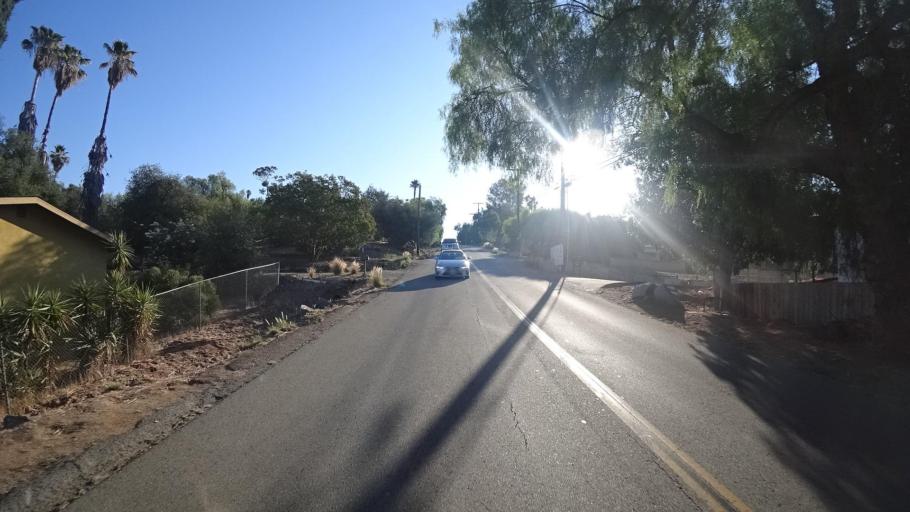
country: US
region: California
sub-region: San Diego County
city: Escondido
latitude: 33.1110
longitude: -117.0681
